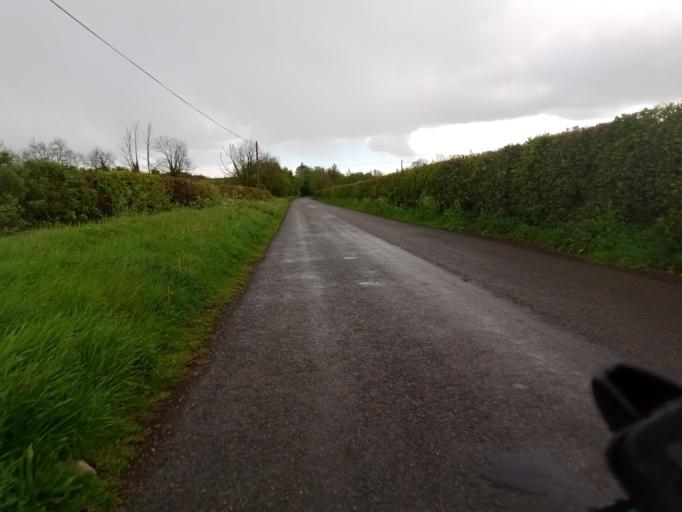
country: IE
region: Leinster
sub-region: Kilkenny
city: Kilkenny
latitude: 52.6770
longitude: -7.2617
